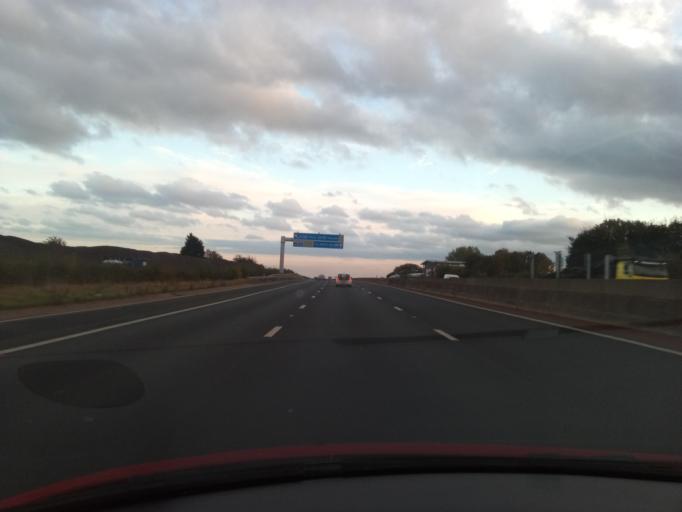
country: GB
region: England
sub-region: North Yorkshire
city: Ripon
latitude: 54.1637
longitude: -1.4476
